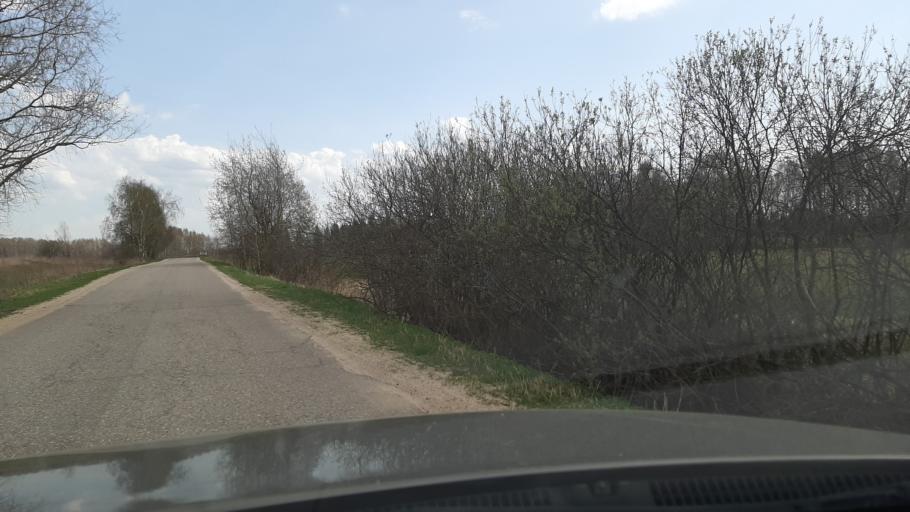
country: RU
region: Ivanovo
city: Furmanov
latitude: 57.2960
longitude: 41.1738
